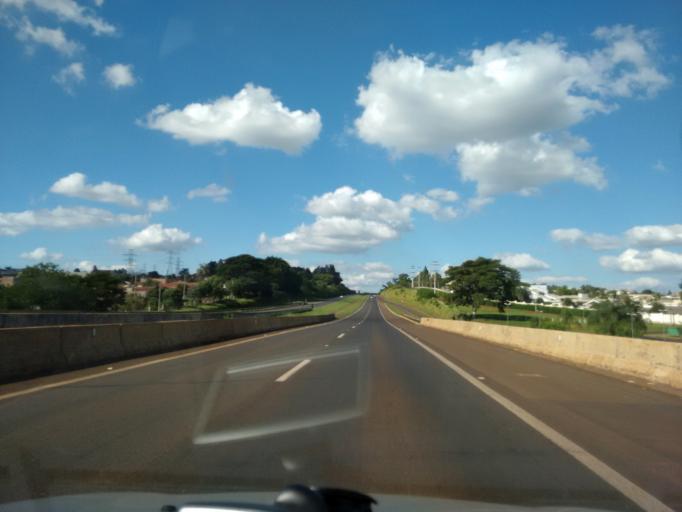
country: BR
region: Sao Paulo
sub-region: Araraquara
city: Araraquara
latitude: -21.8155
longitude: -48.1703
